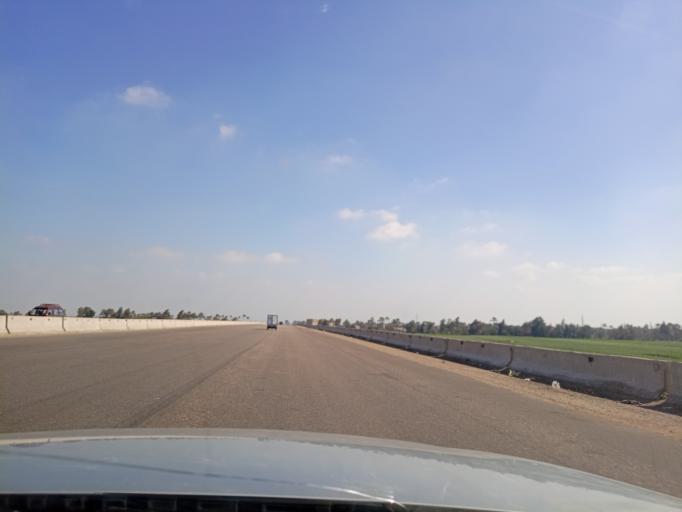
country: EG
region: Eastern Province
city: Mashtul as Suq
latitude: 30.4598
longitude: 31.3493
